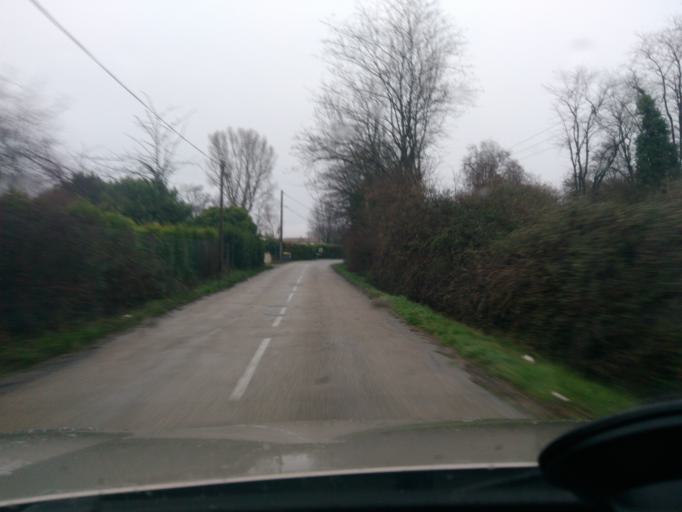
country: FR
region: Rhone-Alpes
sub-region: Departement de la Drome
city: Montelimar
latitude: 44.5378
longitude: 4.7200
